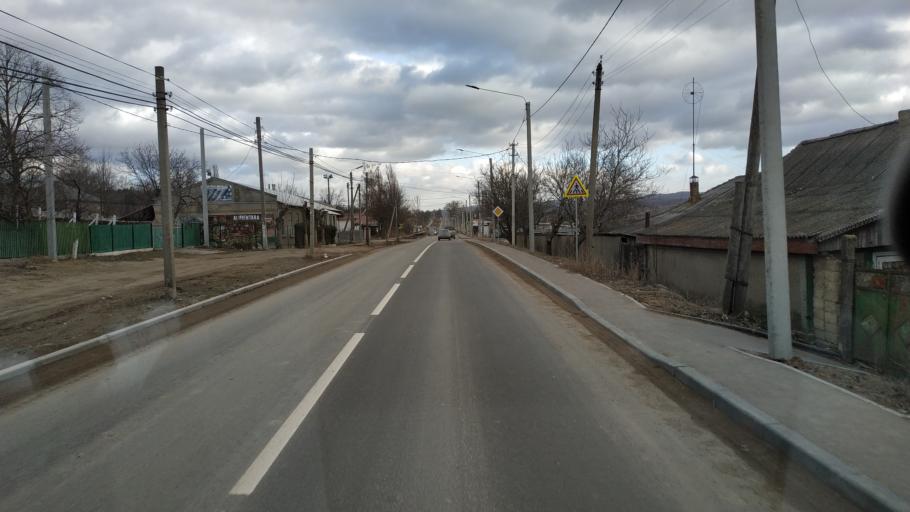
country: MD
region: Calarasi
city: Calarasi
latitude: 47.2823
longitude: 28.2056
